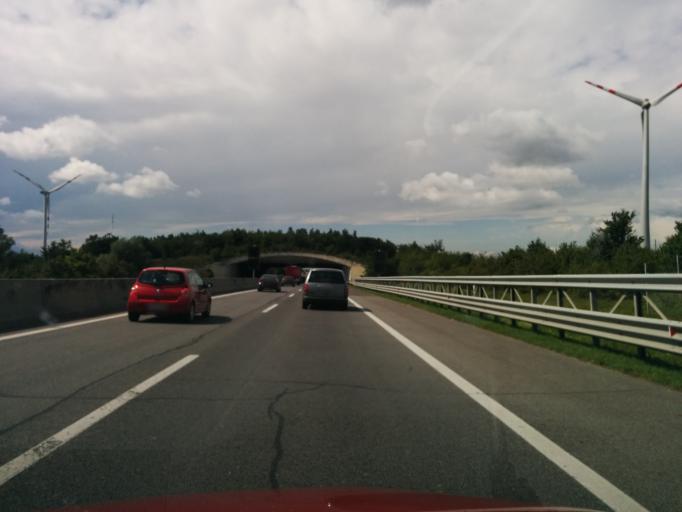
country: AT
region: Burgenland
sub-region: Politischer Bezirk Neusiedl am See
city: Zurndorf
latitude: 47.9401
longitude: 16.9673
